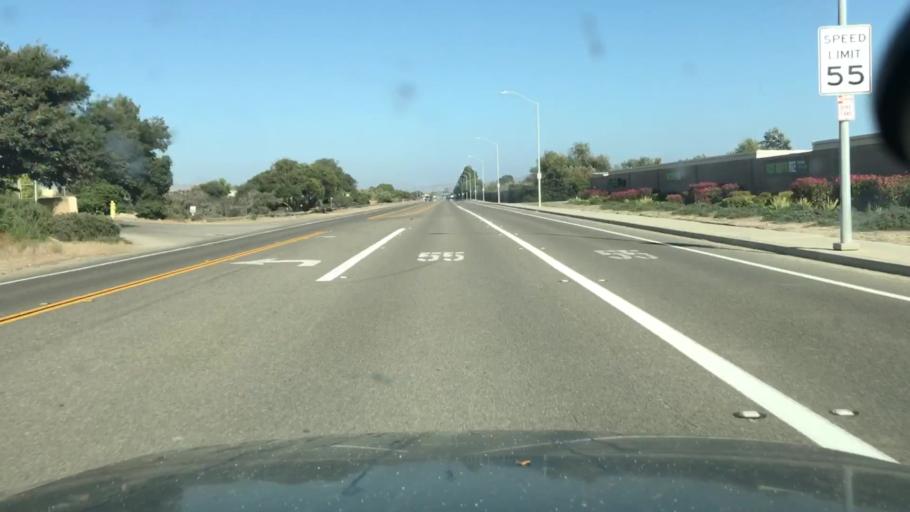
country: US
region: California
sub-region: Santa Barbara County
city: Lompoc
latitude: 34.6611
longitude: -120.4833
